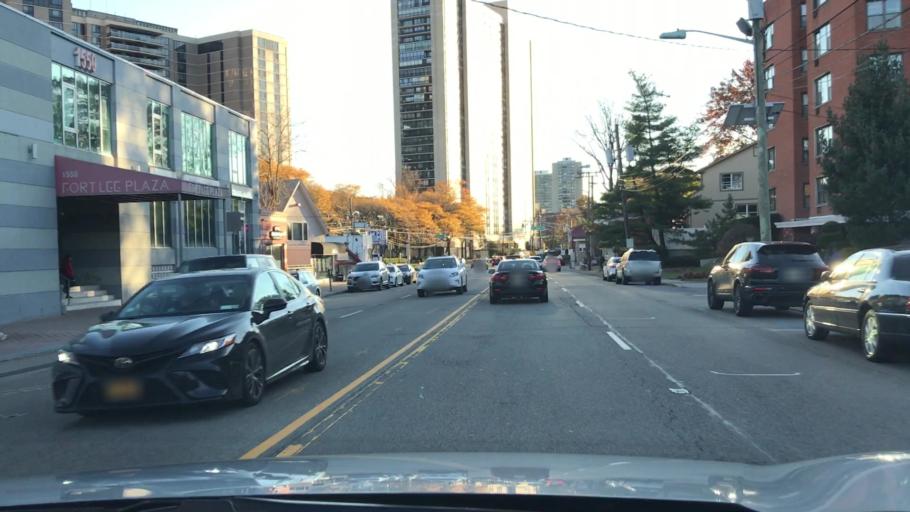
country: US
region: New Jersey
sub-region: Bergen County
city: Fort Lee
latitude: 40.8479
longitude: -73.9708
